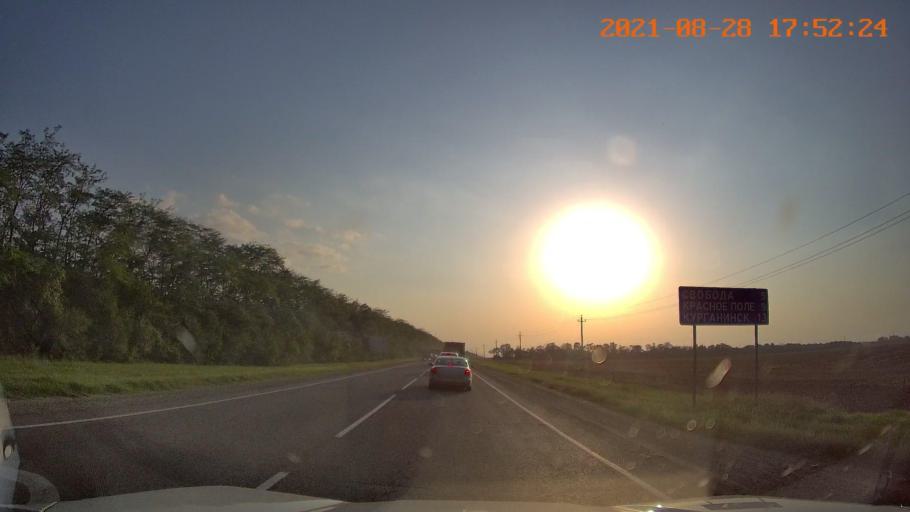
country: RU
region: Krasnodarskiy
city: Konstantinovskaya
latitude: 44.9407
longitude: 40.7754
